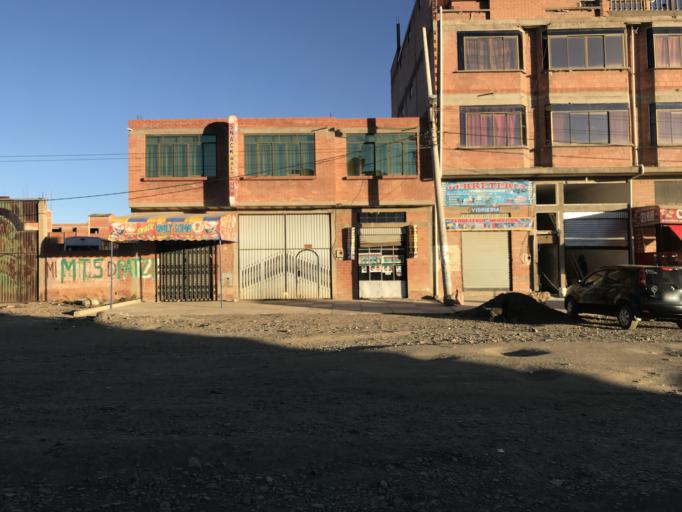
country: BO
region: La Paz
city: La Paz
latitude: -16.5049
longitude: -68.2513
